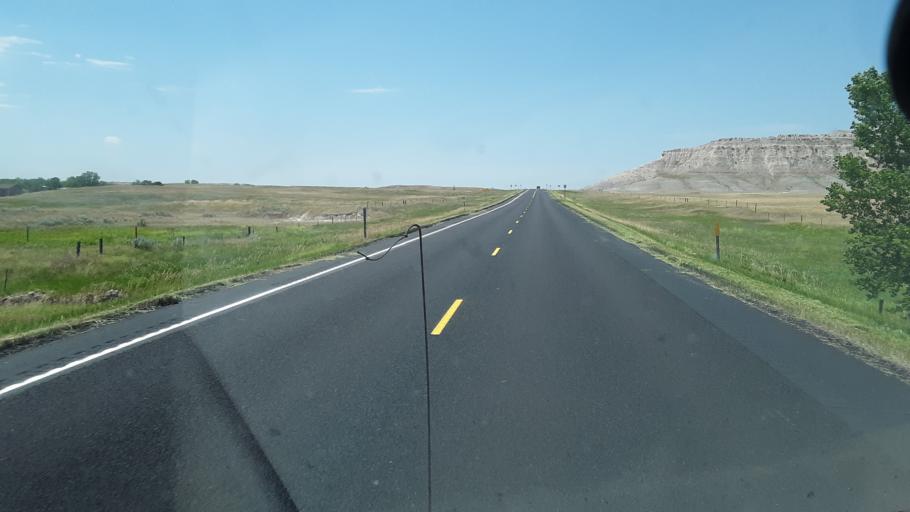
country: US
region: South Dakota
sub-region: Haakon County
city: Philip
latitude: 43.7193
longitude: -102.0139
